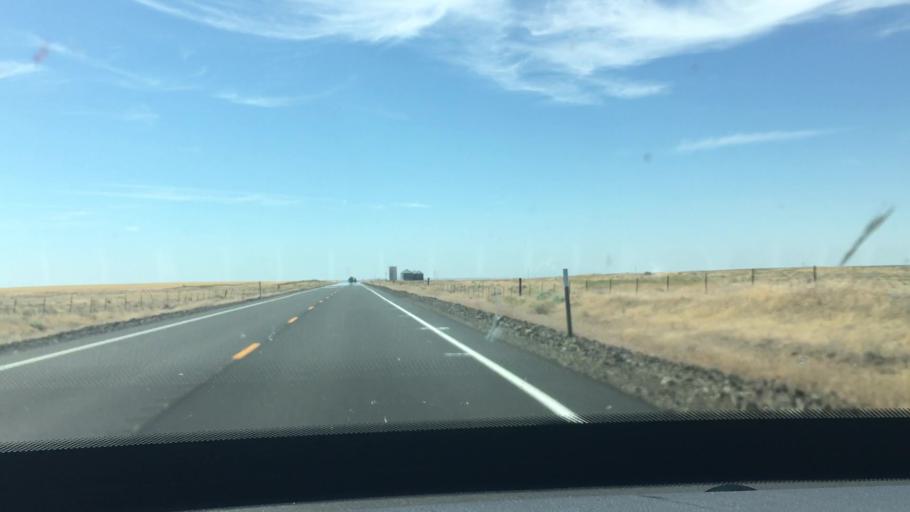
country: US
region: Oregon
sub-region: Sherman County
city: Moro
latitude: 45.2949
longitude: -120.7547
